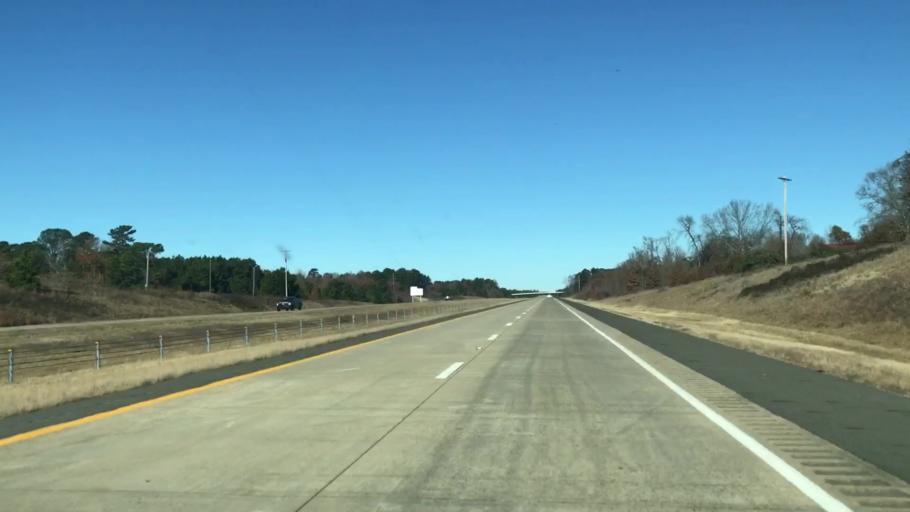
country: US
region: Texas
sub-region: Bowie County
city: Texarkana
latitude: 33.2828
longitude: -93.9110
